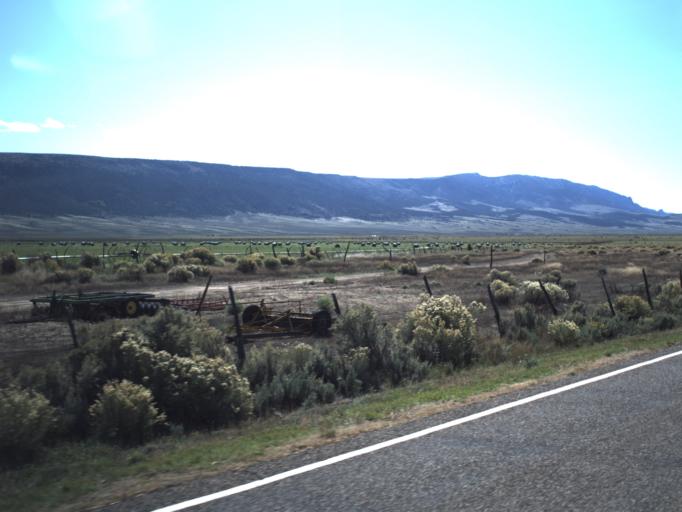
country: US
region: Utah
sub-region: Sevier County
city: Monroe
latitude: 38.4614
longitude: -111.9093
